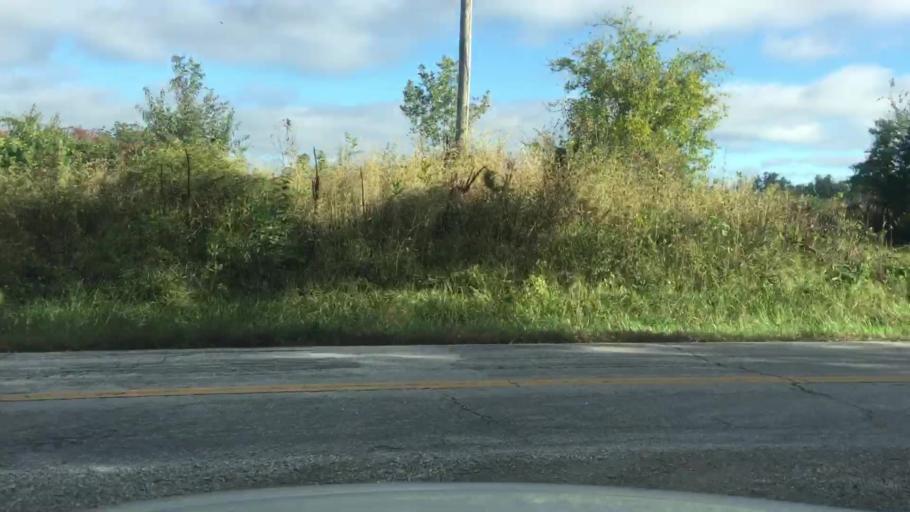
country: US
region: Missouri
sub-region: Howard County
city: New Franklin
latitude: 39.1052
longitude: -92.7791
